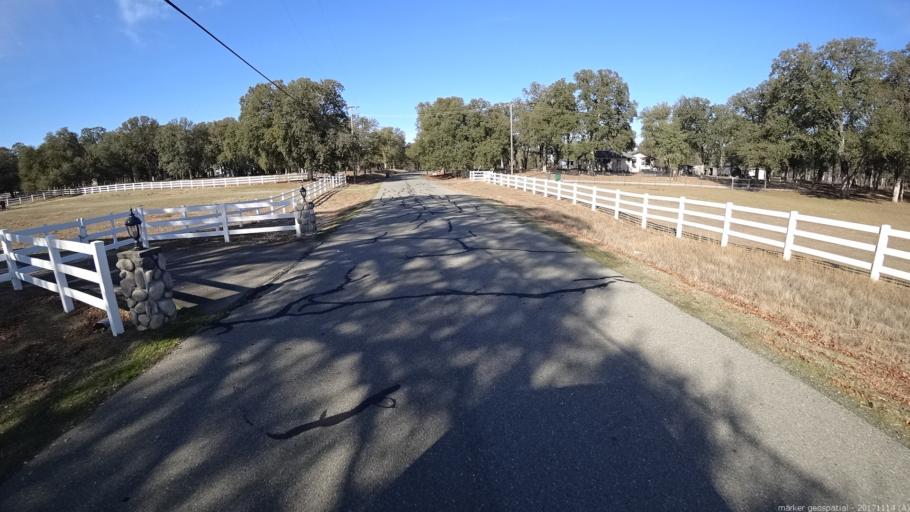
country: US
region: California
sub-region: Shasta County
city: Anderson
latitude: 40.3869
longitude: -122.4518
